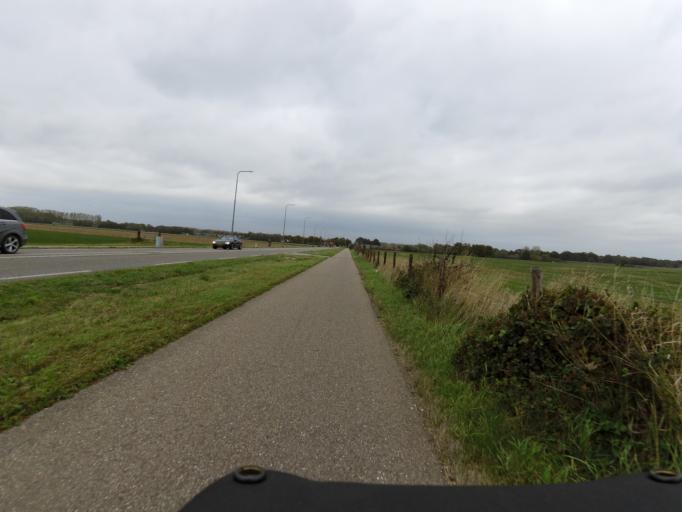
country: NL
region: Gelderland
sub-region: Gemeente Zevenaar
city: Zevenaar
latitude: 51.8997
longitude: 6.1081
